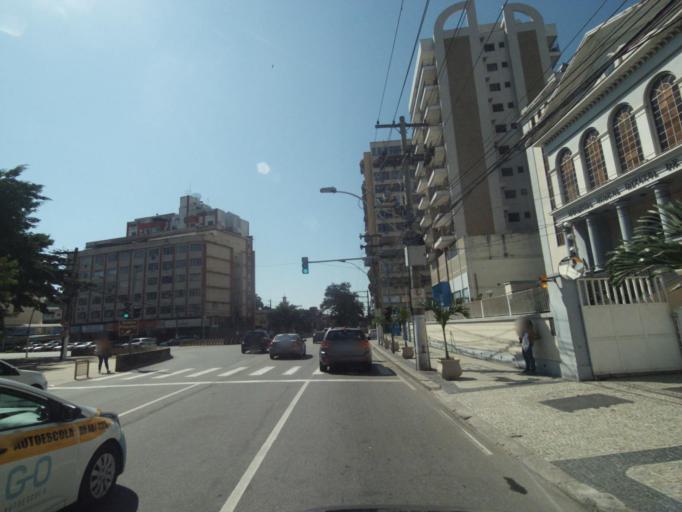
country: BR
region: Rio de Janeiro
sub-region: Niteroi
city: Niteroi
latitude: -22.8942
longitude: -43.1132
